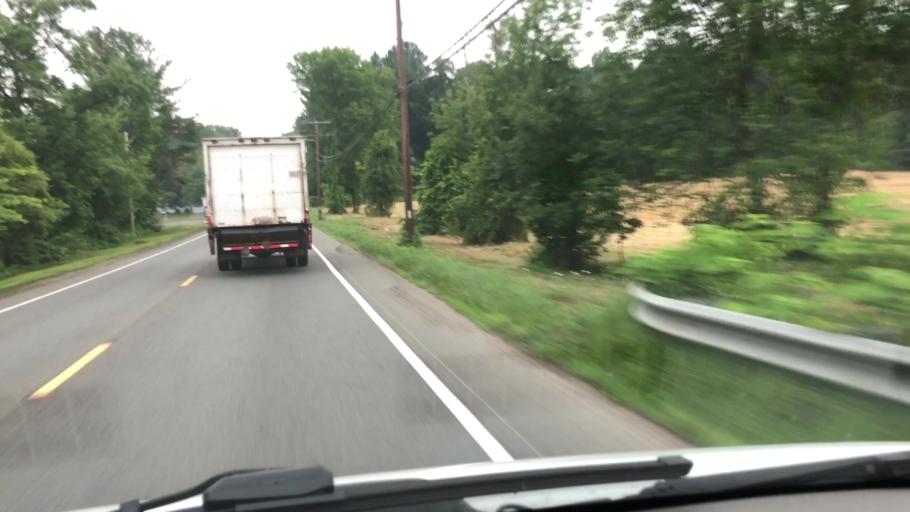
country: US
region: Massachusetts
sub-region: Hampshire County
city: Northampton
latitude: 42.3514
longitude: -72.6905
